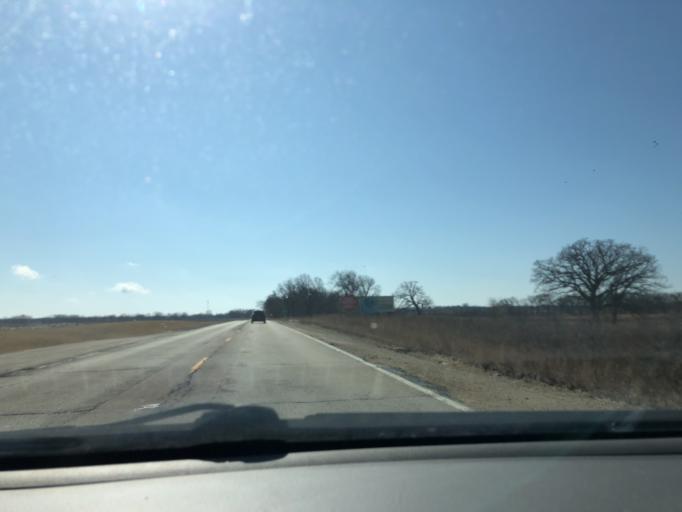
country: US
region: Illinois
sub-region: Kane County
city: Pingree Grove
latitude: 42.1006
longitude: -88.4546
